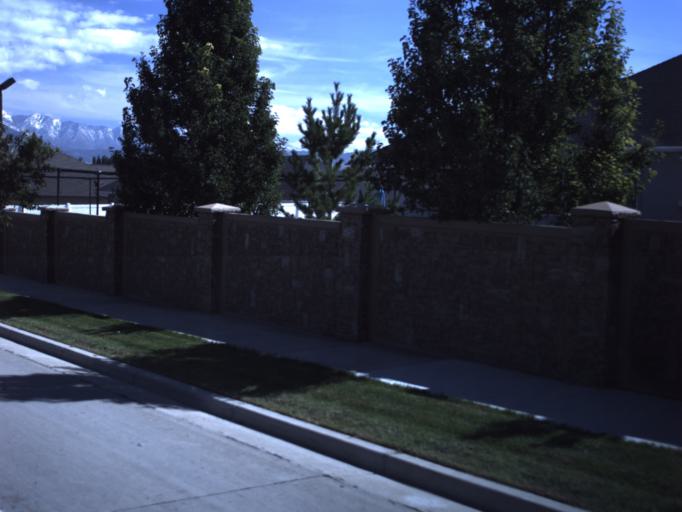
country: US
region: Utah
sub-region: Salt Lake County
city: South Jordan Heights
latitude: 40.5441
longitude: -111.9714
